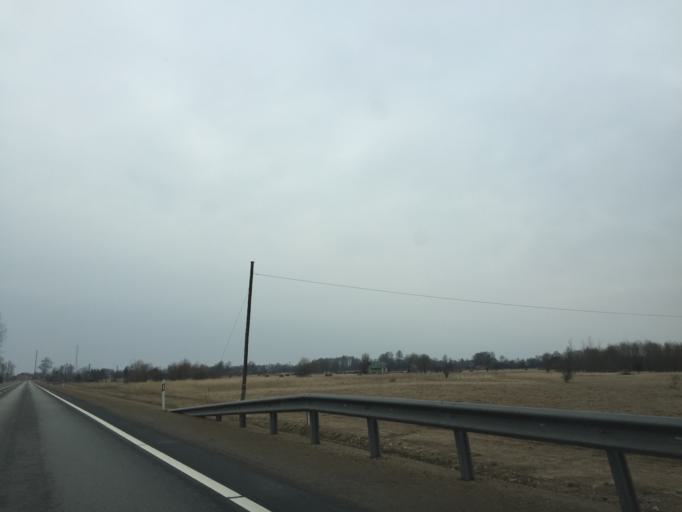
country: LV
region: Salacgrivas
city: Salacgriva
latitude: 57.7374
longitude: 24.3642
